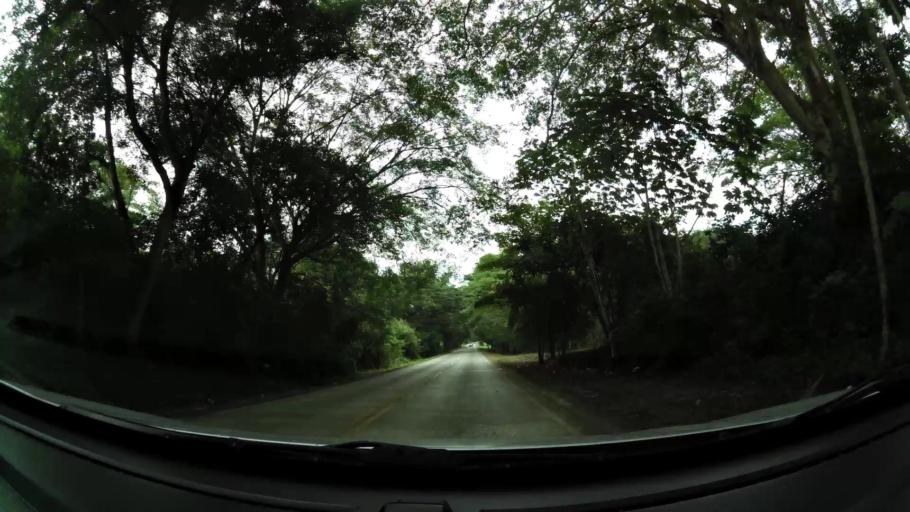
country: CR
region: Guanacaste
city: Juntas
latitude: 10.2536
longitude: -85.0529
